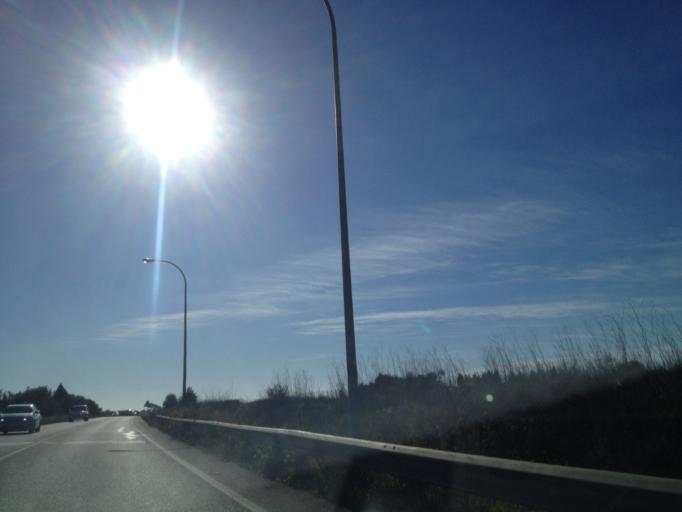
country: ES
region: Balearic Islands
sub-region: Illes Balears
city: Petra
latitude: 39.6166
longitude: 3.1222
